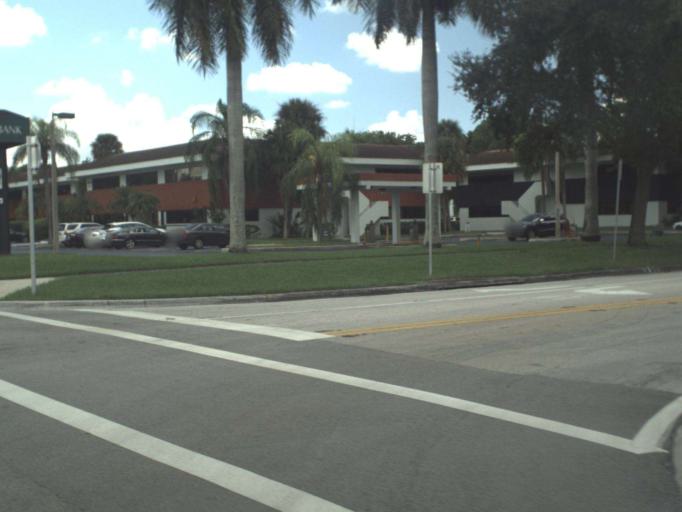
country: US
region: Florida
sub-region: Miami-Dade County
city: The Crossings
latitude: 25.6836
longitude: -80.4166
